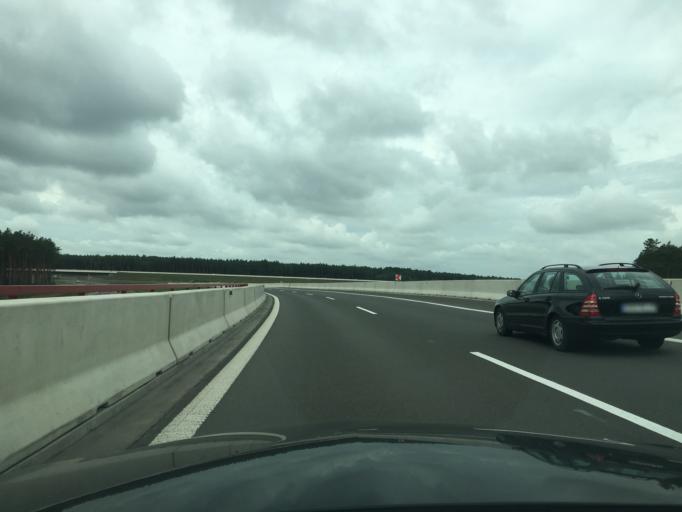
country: DE
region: Brandenburg
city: Kremmen
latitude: 52.7118
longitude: 13.0207
